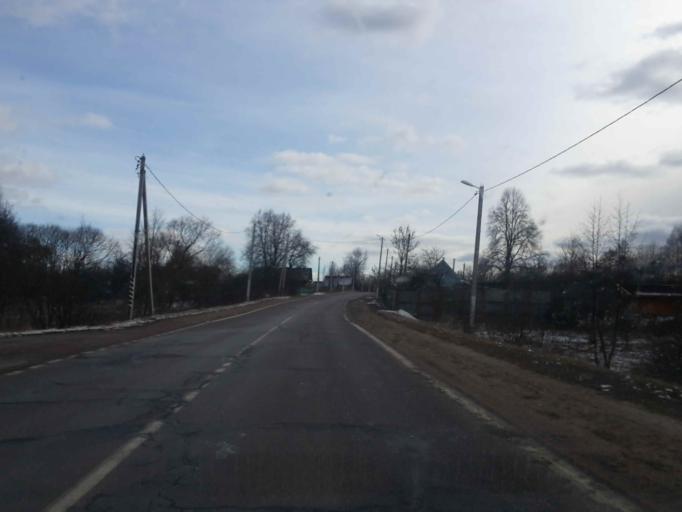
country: BY
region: Vitebsk
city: Pastavy
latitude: 55.0077
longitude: 26.8827
